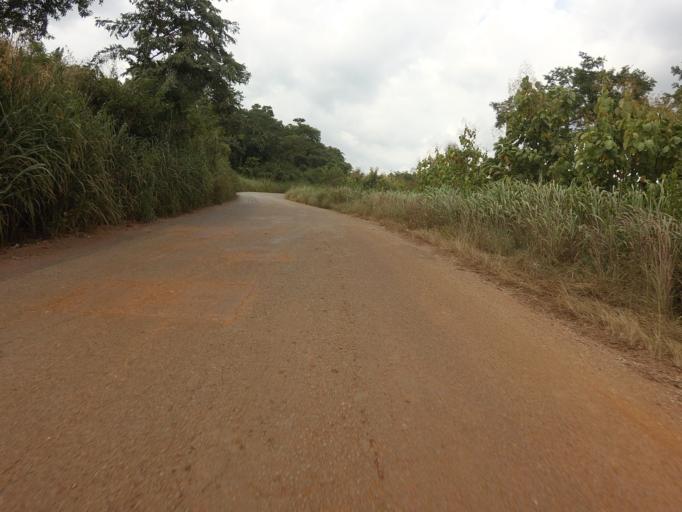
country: GH
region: Volta
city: Ho
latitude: 6.6774
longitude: 0.3526
